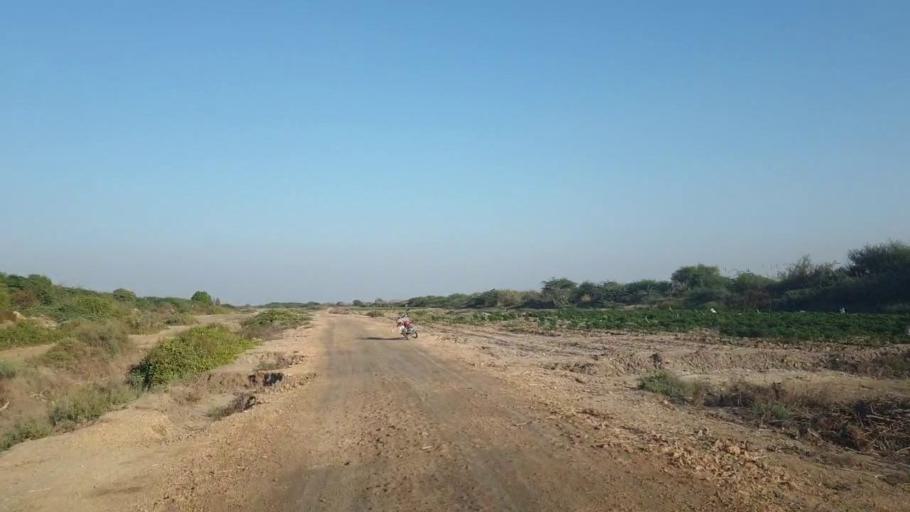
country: PK
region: Sindh
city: Mirpur Sakro
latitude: 24.5352
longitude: 67.5290
